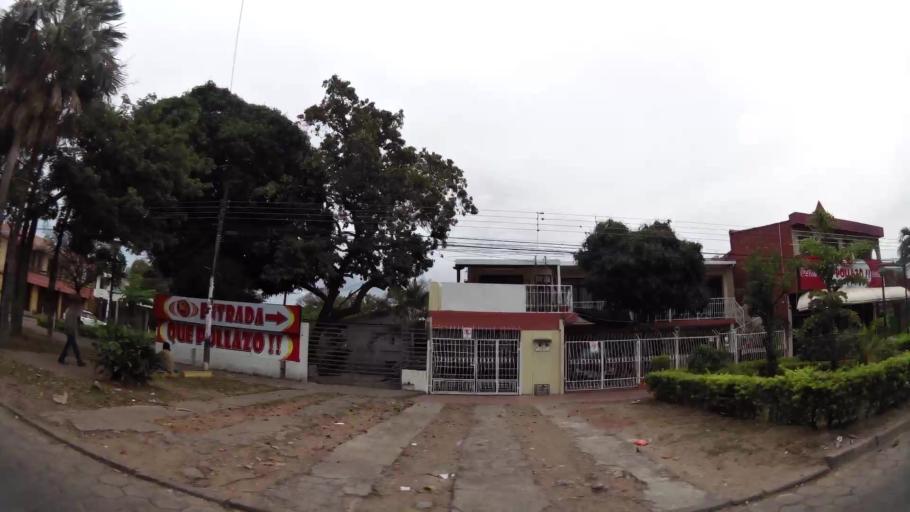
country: BO
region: Santa Cruz
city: Santa Cruz de la Sierra
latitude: -17.7983
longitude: -63.1883
